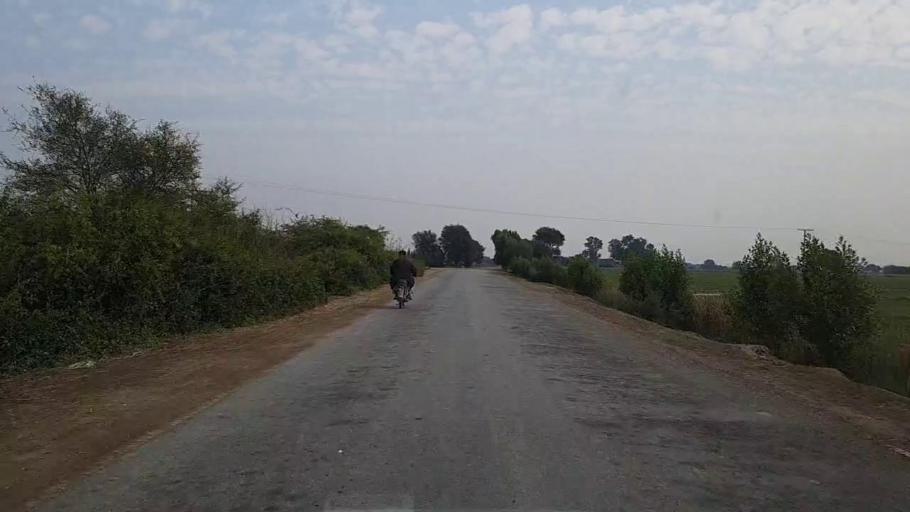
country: PK
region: Sindh
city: Mirwah Gorchani
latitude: 25.3982
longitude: 69.0684
